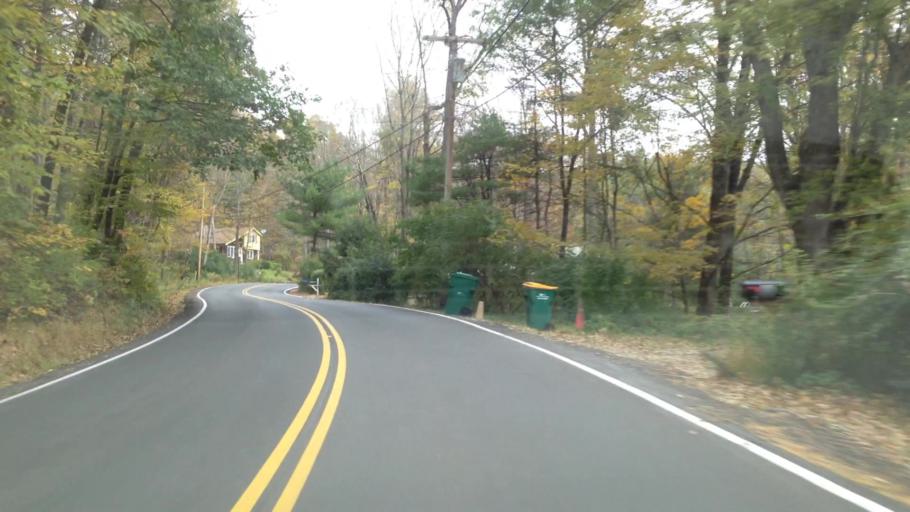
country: US
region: New York
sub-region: Ulster County
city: Tillson
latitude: 41.8235
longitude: -74.0139
